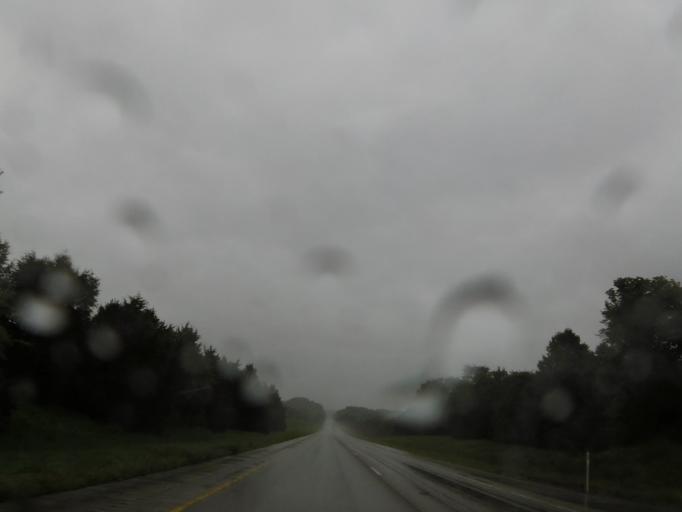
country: US
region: Illinois
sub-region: Johnson County
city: Vienna
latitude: 37.4697
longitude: -88.8911
